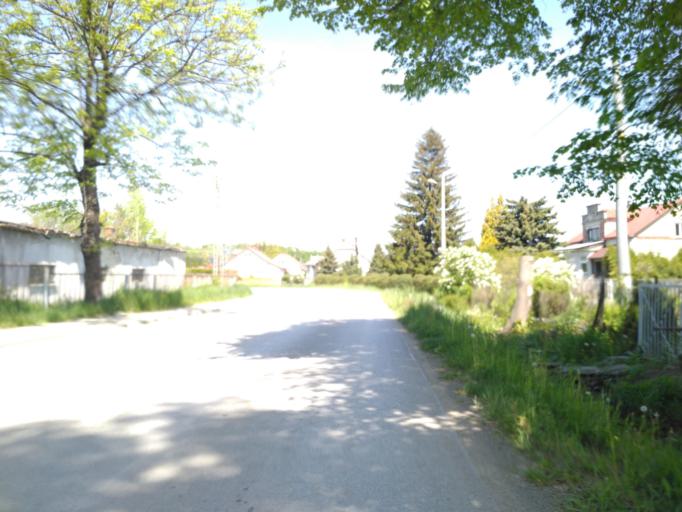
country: PL
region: Subcarpathian Voivodeship
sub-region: Powiat krosnienski
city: Dukla
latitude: 49.5534
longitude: 21.6897
